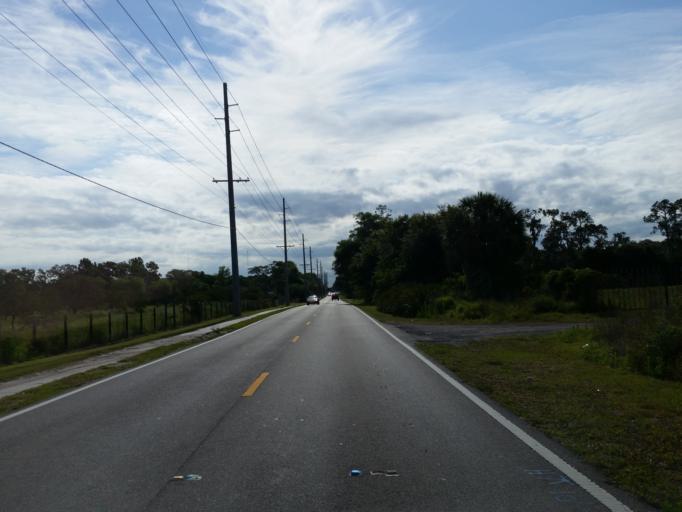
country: US
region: Florida
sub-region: Hillsborough County
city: Riverview
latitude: 27.8352
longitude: -82.3376
